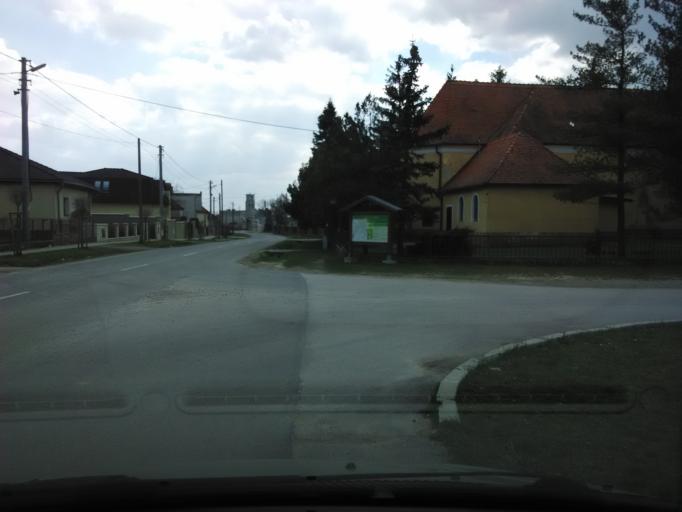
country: SK
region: Nitriansky
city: Zlate Moravce
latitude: 48.4152
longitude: 18.3039
